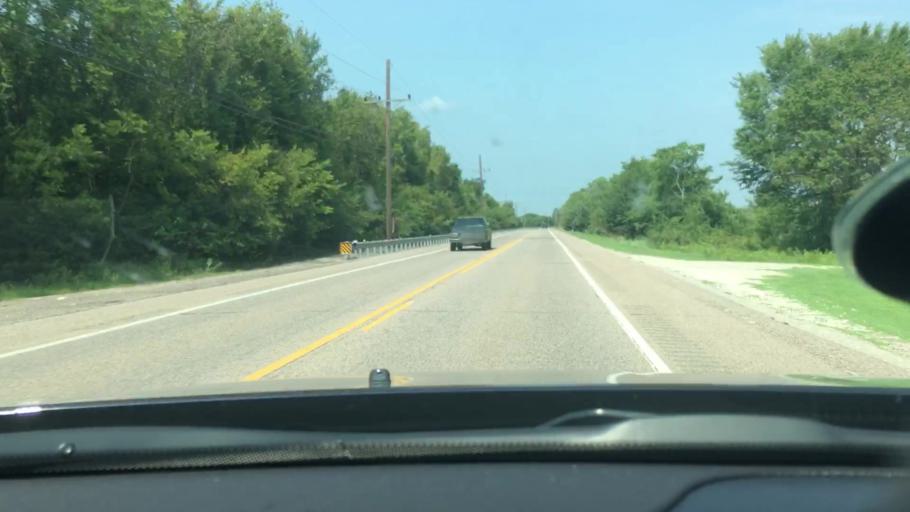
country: US
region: Texas
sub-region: Grayson County
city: Preston
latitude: 33.9988
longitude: -96.5873
